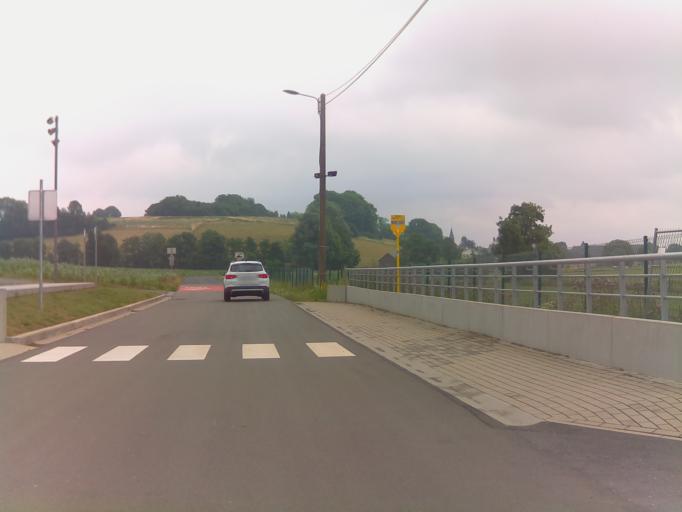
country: LU
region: Luxembourg
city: Eischen
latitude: 49.6490
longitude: 5.8757
